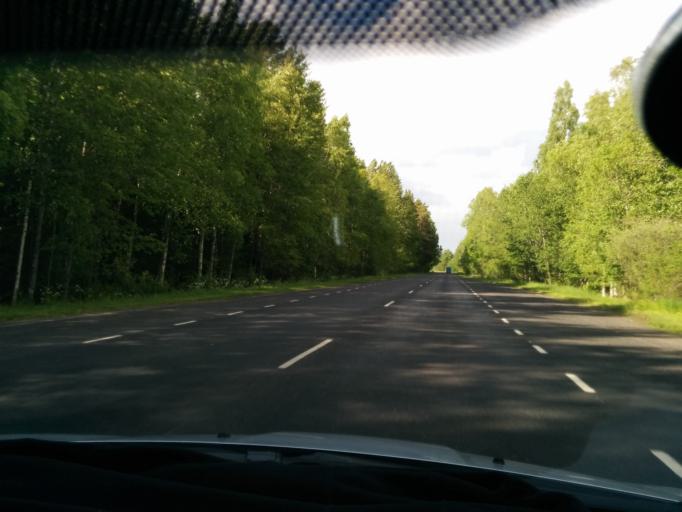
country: EE
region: Harju
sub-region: Loksa linn
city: Loksa
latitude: 59.5615
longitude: 25.7246
